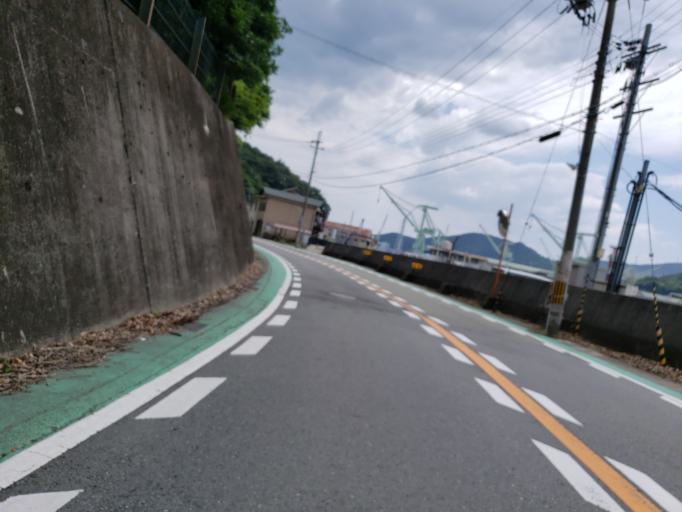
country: JP
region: Hyogo
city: Aioi
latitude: 34.7963
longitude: 134.4699
